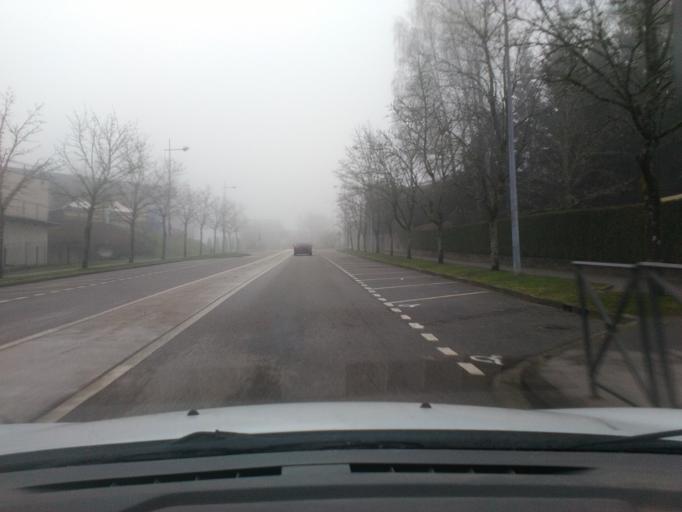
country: FR
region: Lorraine
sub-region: Departement des Vosges
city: Epinal
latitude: 48.1888
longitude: 6.4628
